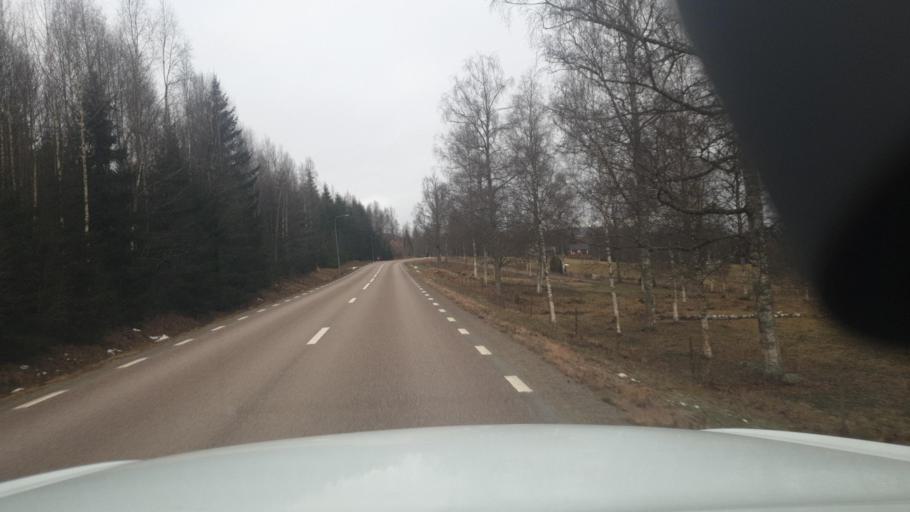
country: SE
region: Vaermland
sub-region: Sunne Kommun
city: Sunne
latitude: 59.8793
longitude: 12.9299
